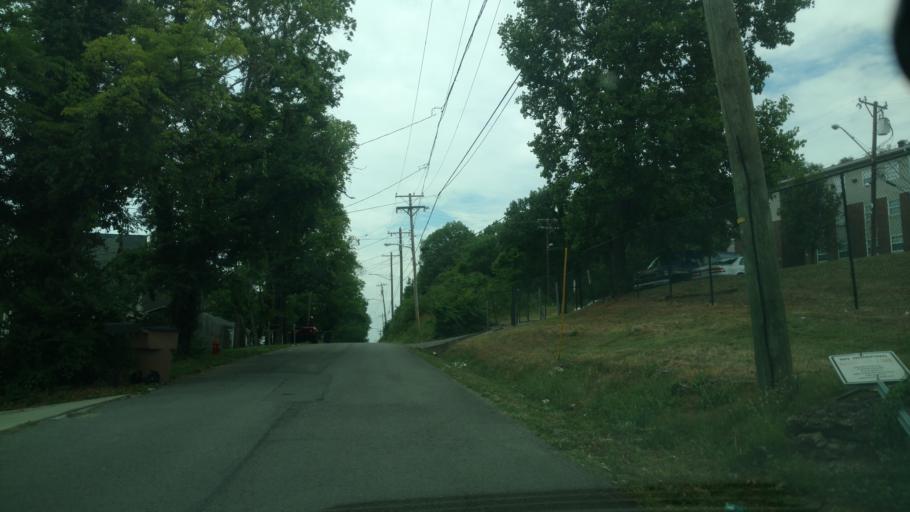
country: US
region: Tennessee
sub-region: Davidson County
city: Nashville
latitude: 36.1918
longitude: -86.7288
